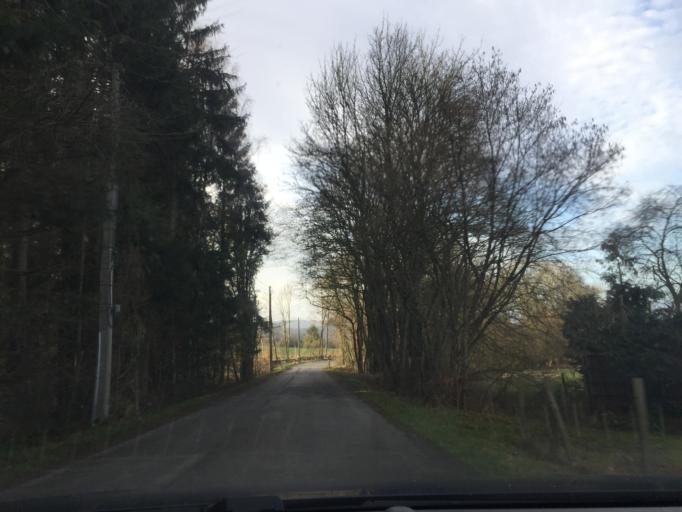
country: BE
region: Wallonia
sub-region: Province du Luxembourg
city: Hotton
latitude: 50.2937
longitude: 5.4884
